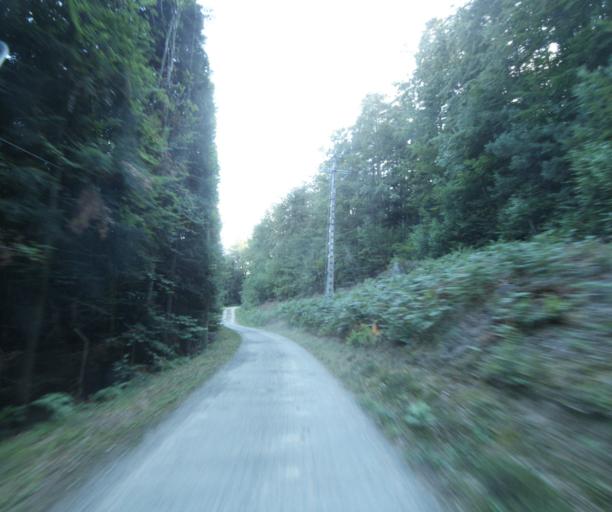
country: FR
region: Lorraine
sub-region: Departement des Vosges
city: Chantraine
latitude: 48.1425
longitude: 6.4287
